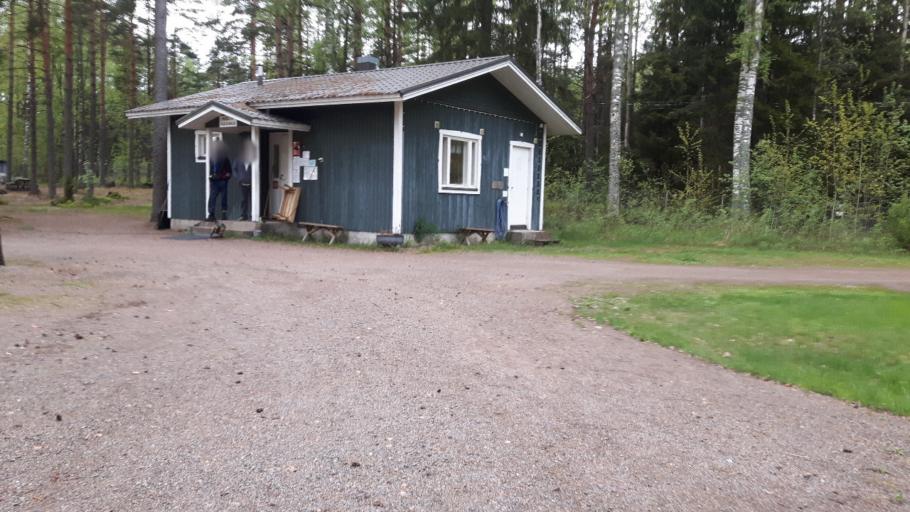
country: FI
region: Kymenlaakso
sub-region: Kotka-Hamina
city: Hamina
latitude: 60.5257
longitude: 27.2552
